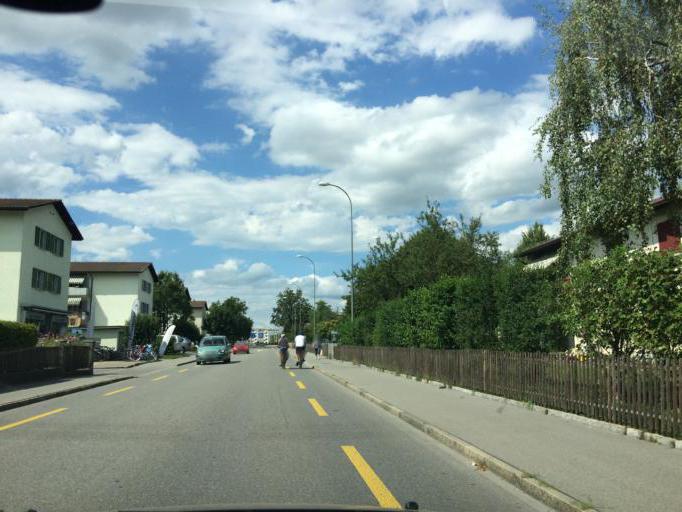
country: CH
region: Bern
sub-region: Thun District
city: Thun
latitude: 46.7419
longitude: 7.6144
